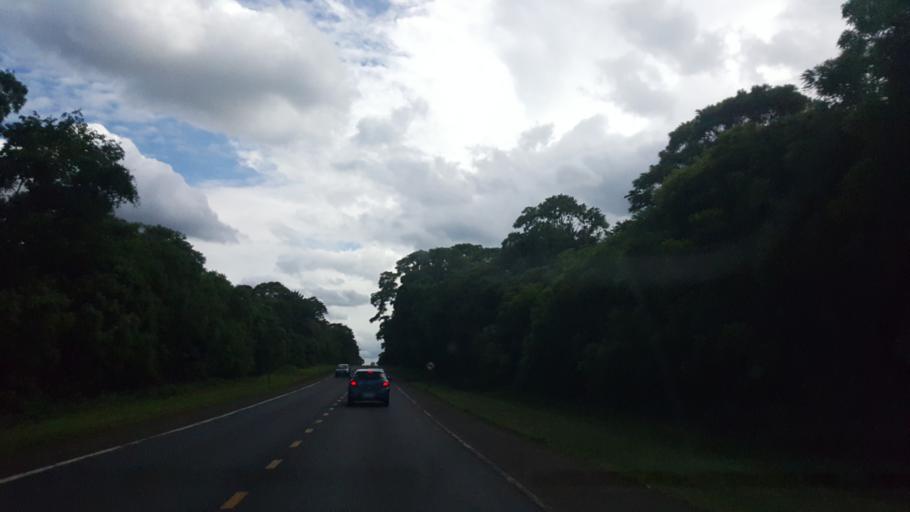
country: AR
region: Misiones
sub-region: Departamento de Iguazu
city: Puerto Iguazu
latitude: -25.7067
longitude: -54.5160
